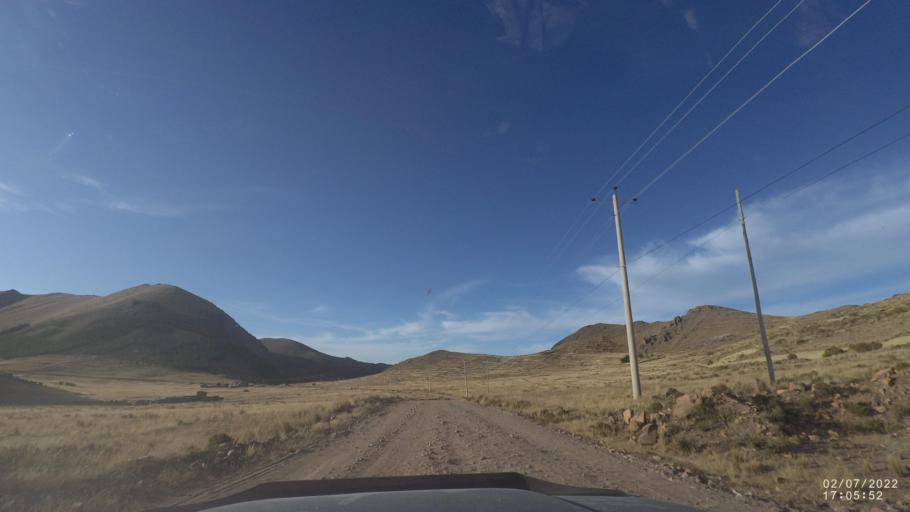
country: BO
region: Cochabamba
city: Irpa Irpa
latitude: -17.9030
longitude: -66.5581
